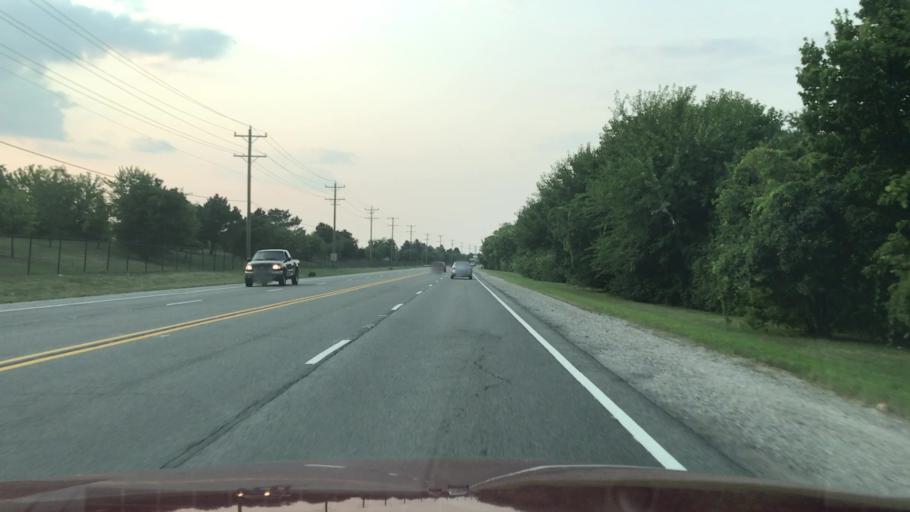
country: US
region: Illinois
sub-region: Will County
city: Lockport
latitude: 41.6158
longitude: -88.0770
